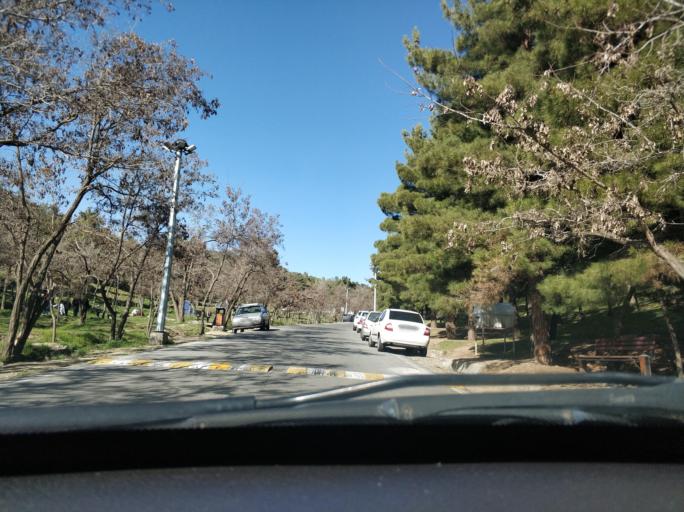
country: IR
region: Tehran
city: Tajrish
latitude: 35.7893
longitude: 51.5601
